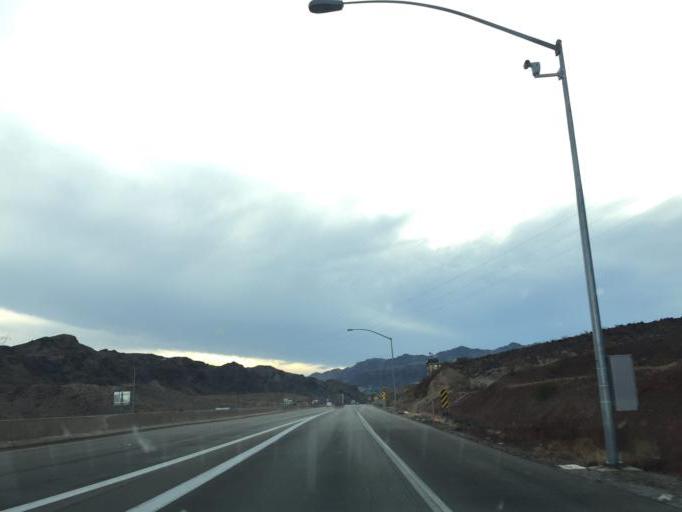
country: US
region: Nevada
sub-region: Clark County
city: Boulder City
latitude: 36.0109
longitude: -114.7774
